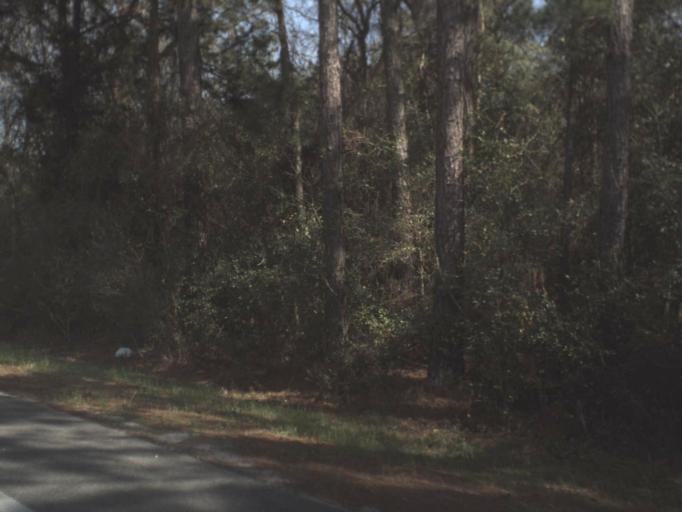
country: US
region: Florida
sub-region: Wakulla County
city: Crawfordville
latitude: 30.0745
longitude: -84.4337
